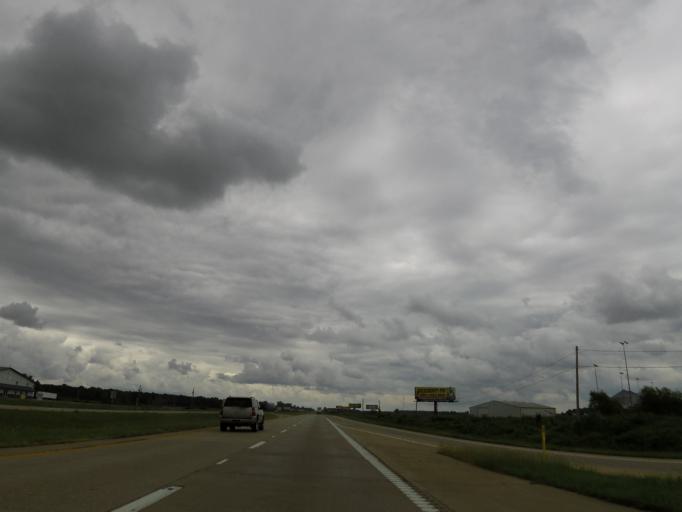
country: US
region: Missouri
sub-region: Mississippi County
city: Charleston
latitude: 36.9227
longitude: -89.3164
